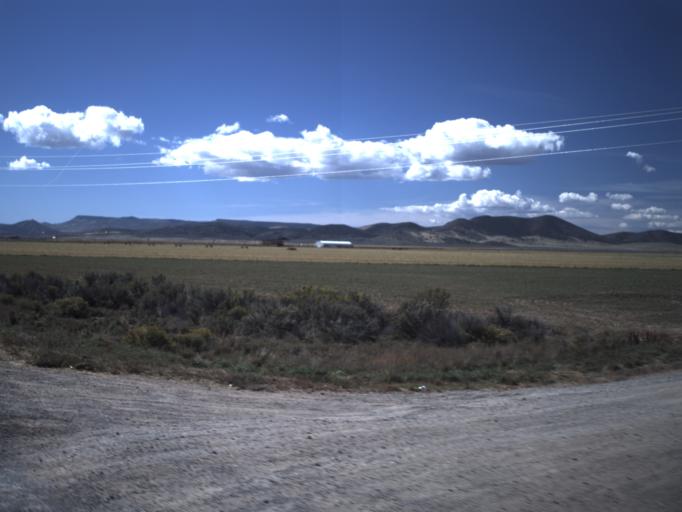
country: US
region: Utah
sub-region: Washington County
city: Enterprise
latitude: 37.6704
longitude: -113.6610
